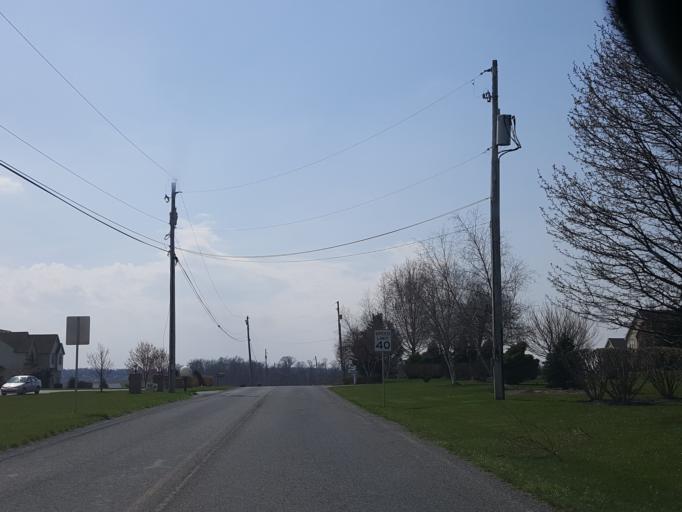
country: US
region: Pennsylvania
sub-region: Lebanon County
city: Campbelltown
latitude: 40.2920
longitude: -76.5428
